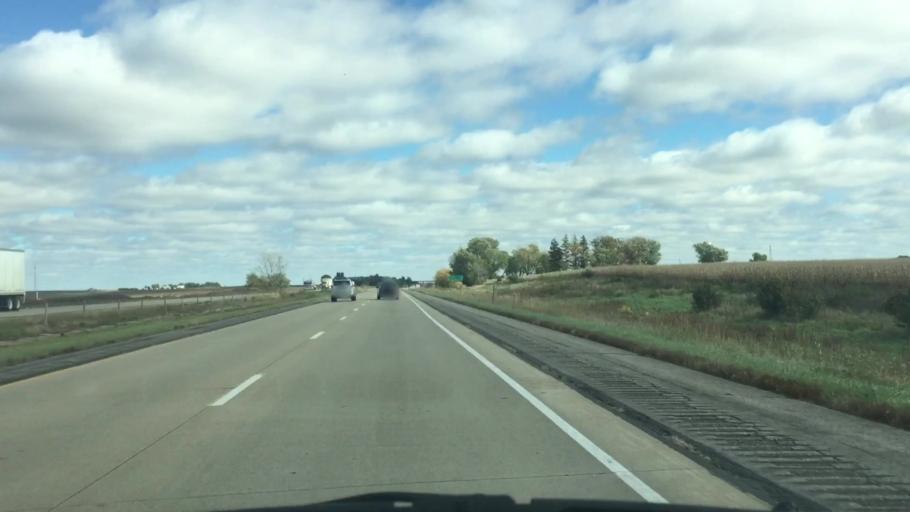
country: US
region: Iowa
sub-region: Poweshiek County
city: Brooklyn
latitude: 41.6962
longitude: -92.2653
